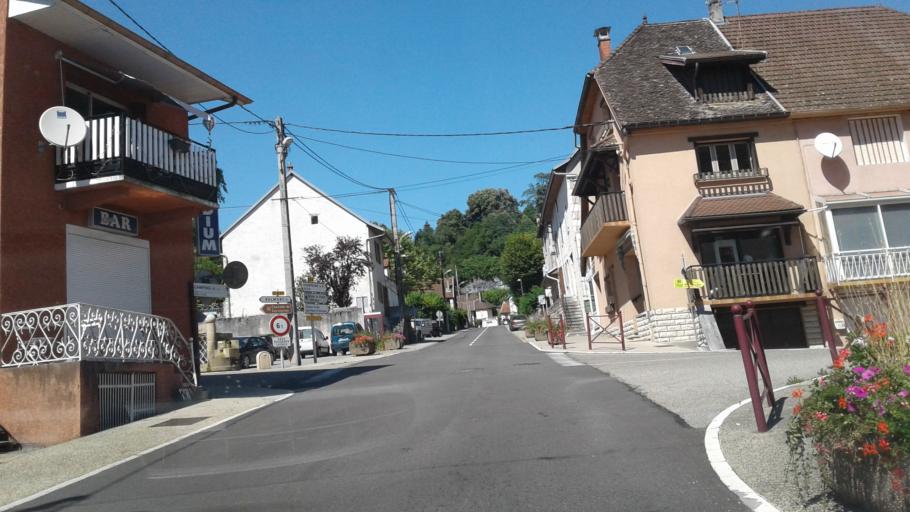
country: FR
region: Rhone-Alpes
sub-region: Departement de l'Ain
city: Artemare
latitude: 45.8742
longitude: 5.6920
